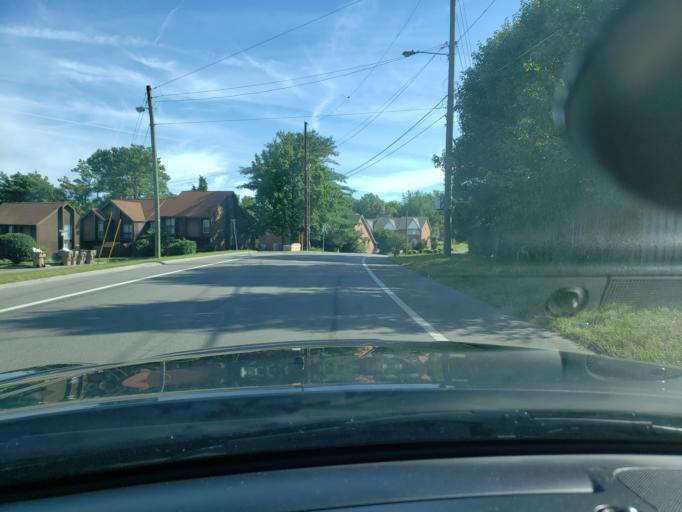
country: US
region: Tennessee
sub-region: Williamson County
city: Nolensville
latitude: 36.0414
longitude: -86.6722
